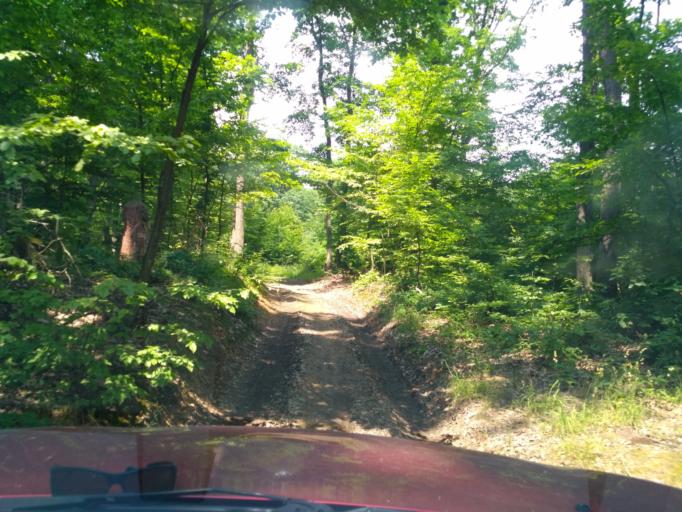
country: SK
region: Kosicky
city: Moldava nad Bodvou
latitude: 48.6352
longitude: 21.0426
